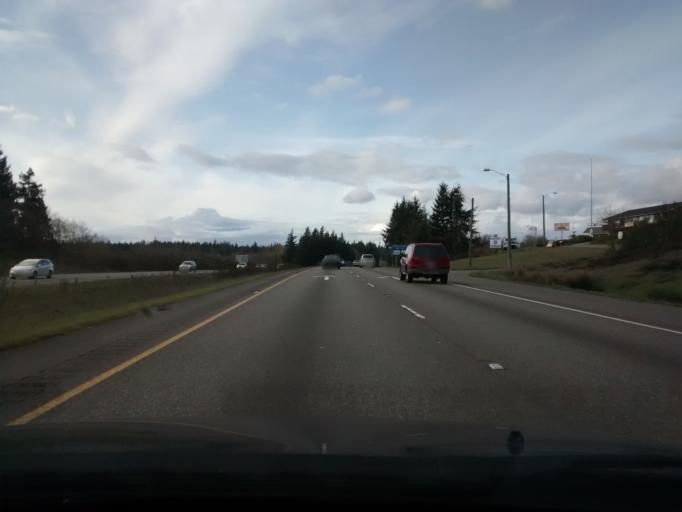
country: US
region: Washington
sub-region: Pierce County
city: Gig Harbor
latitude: 47.3362
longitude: -122.6039
